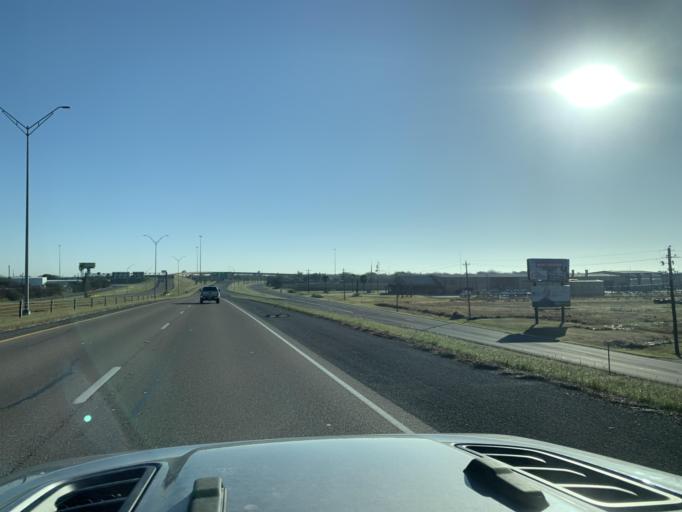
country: US
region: Texas
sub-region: Nueces County
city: Corpus Christi
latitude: 27.7816
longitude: -97.4767
